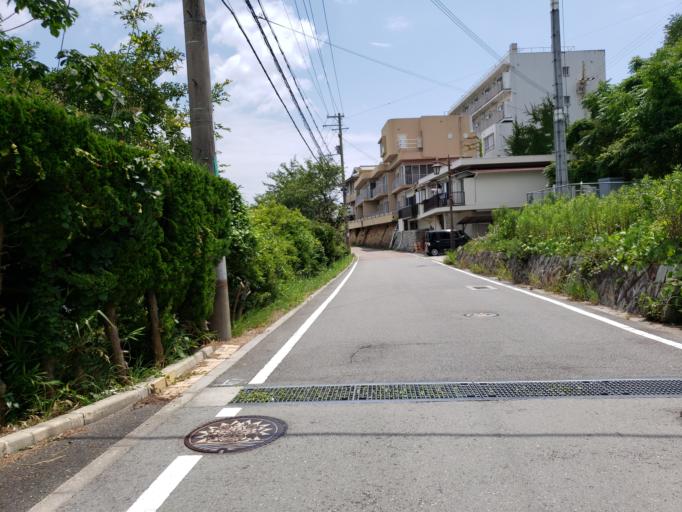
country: JP
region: Hyogo
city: Kariya
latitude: 34.7291
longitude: 134.4104
